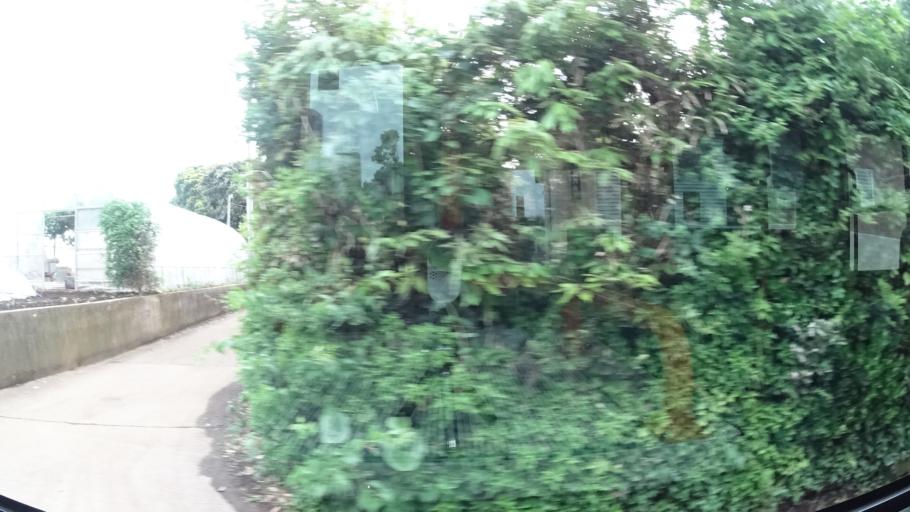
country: JP
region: Kanagawa
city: Miura
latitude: 35.1447
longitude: 139.6533
